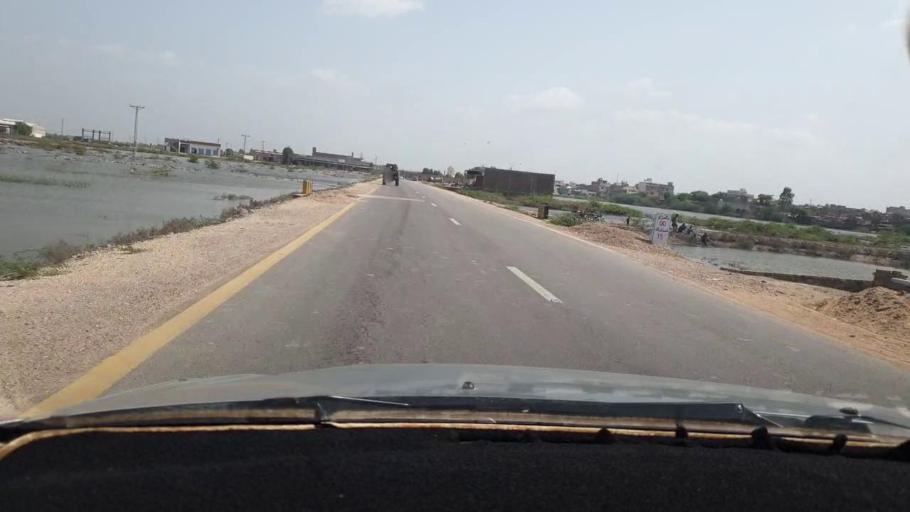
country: PK
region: Sindh
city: Digri
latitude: 25.1640
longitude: 69.1153
